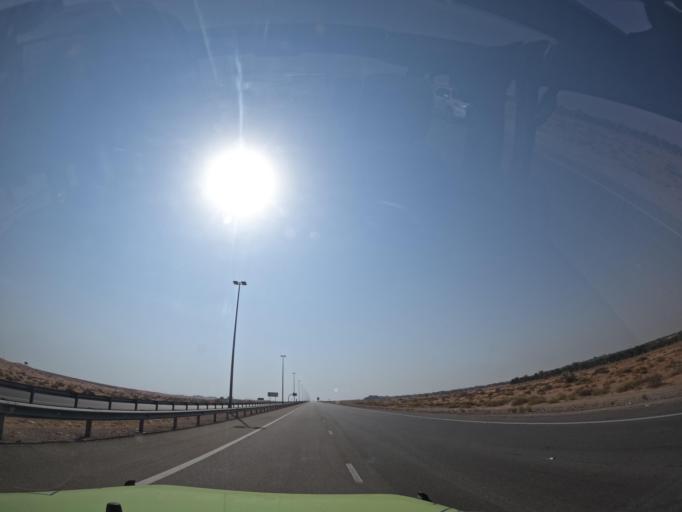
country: OM
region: Al Buraimi
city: Al Buraymi
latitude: 24.4057
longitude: 55.7083
